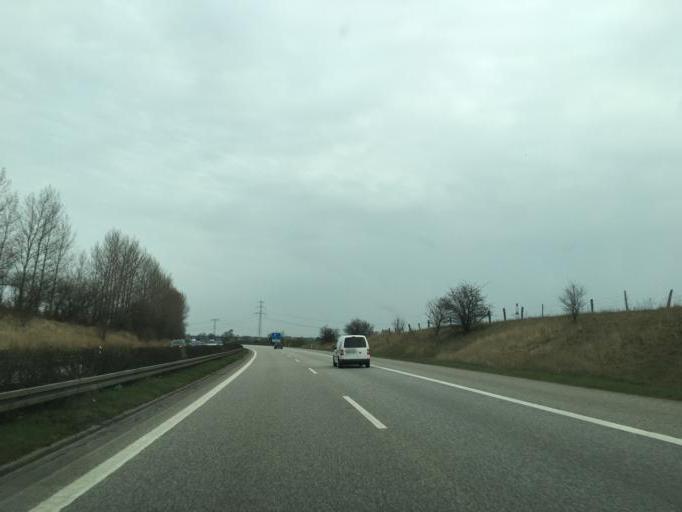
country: DE
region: Mecklenburg-Vorpommern
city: Bentwisch
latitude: 54.0934
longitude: 12.2010
